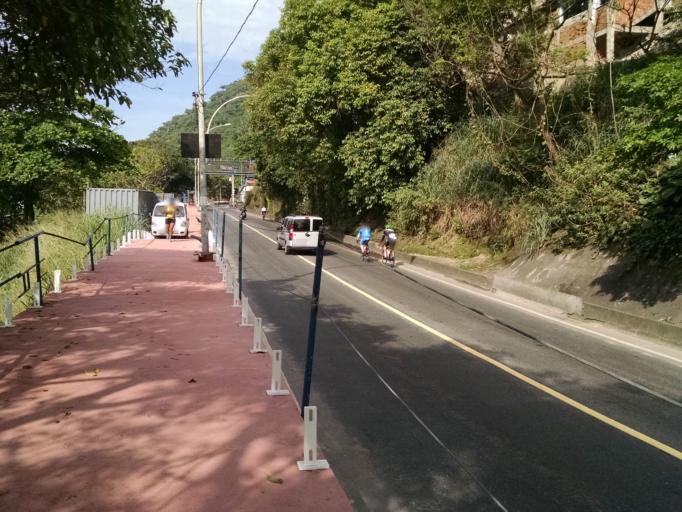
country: BR
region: Rio de Janeiro
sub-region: Rio De Janeiro
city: Rio de Janeiro
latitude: -22.9965
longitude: -43.2360
